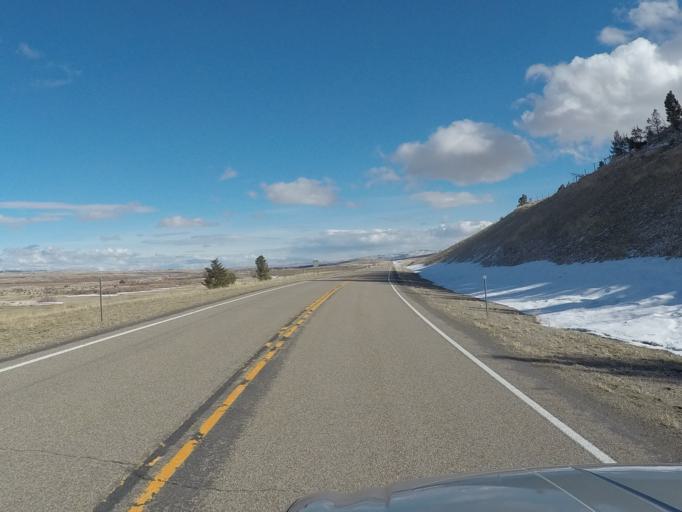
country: US
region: Montana
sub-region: Meagher County
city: White Sulphur Springs
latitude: 46.5389
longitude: -110.4395
